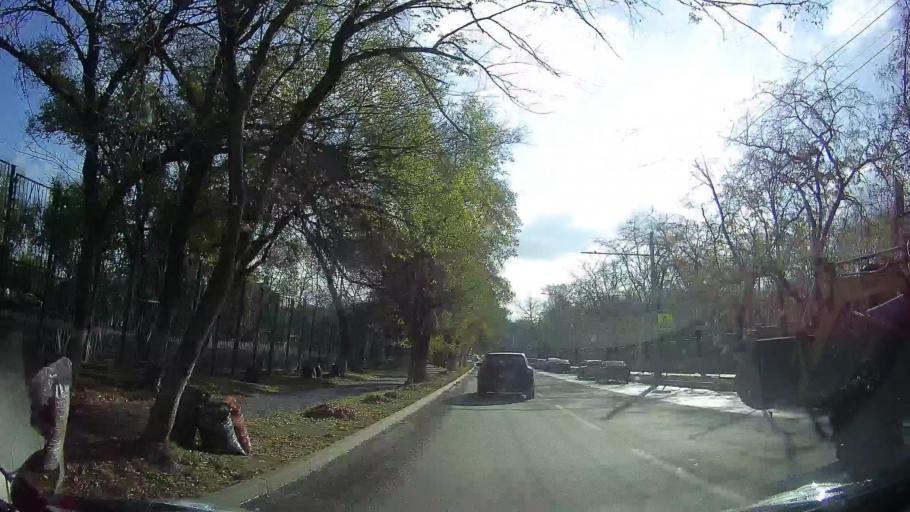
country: RU
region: Rostov
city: Severnyy
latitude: 47.2608
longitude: 39.6735
